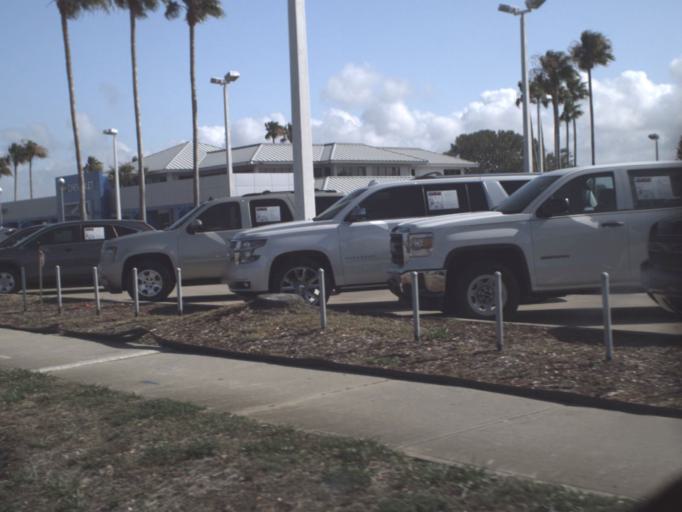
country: US
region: Florida
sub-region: Brevard County
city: Melbourne
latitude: 28.0996
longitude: -80.6129
